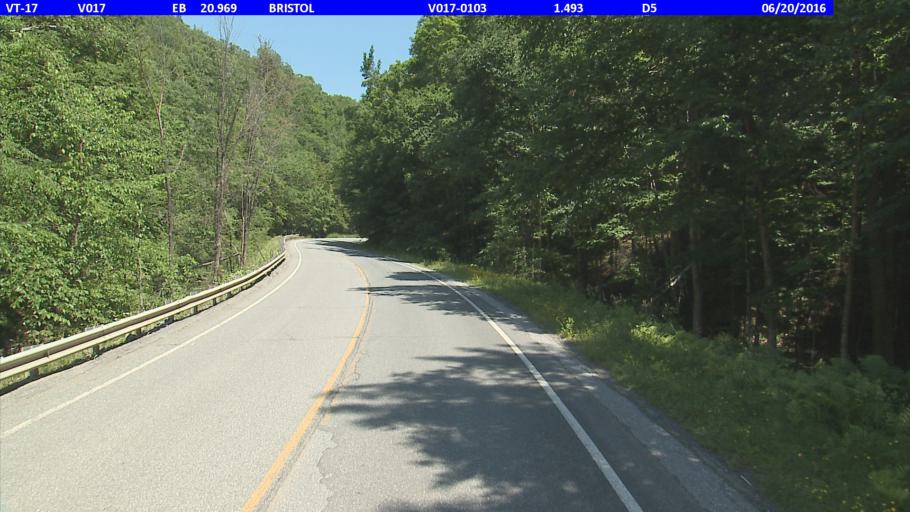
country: US
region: Vermont
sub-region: Addison County
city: Bristol
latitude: 44.1607
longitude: -73.0331
